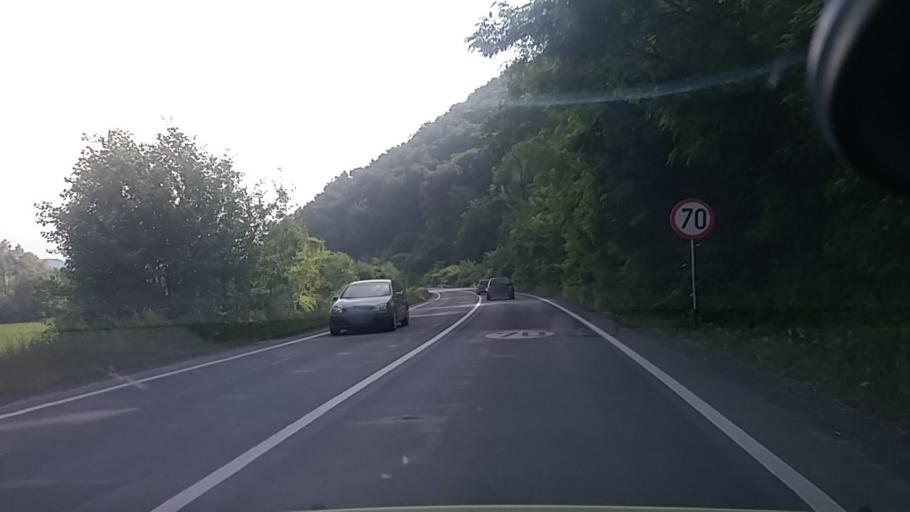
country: RO
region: Arad
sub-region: Comuna Barzava
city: Barzava
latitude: 46.1111
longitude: 21.9525
